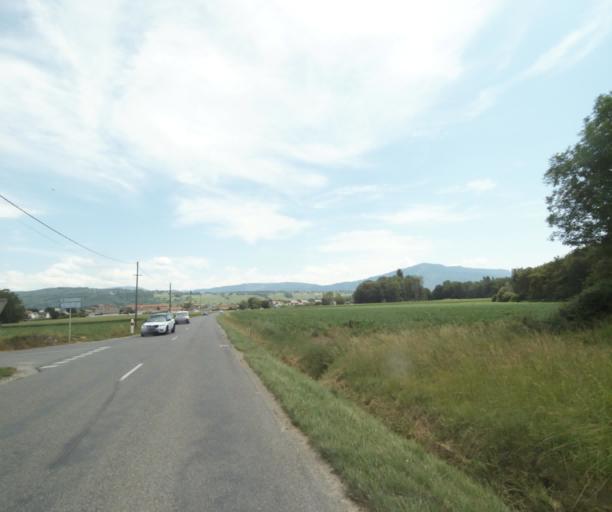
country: FR
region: Rhone-Alpes
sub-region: Departement de la Haute-Savoie
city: Douvaine
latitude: 46.3097
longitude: 6.2847
